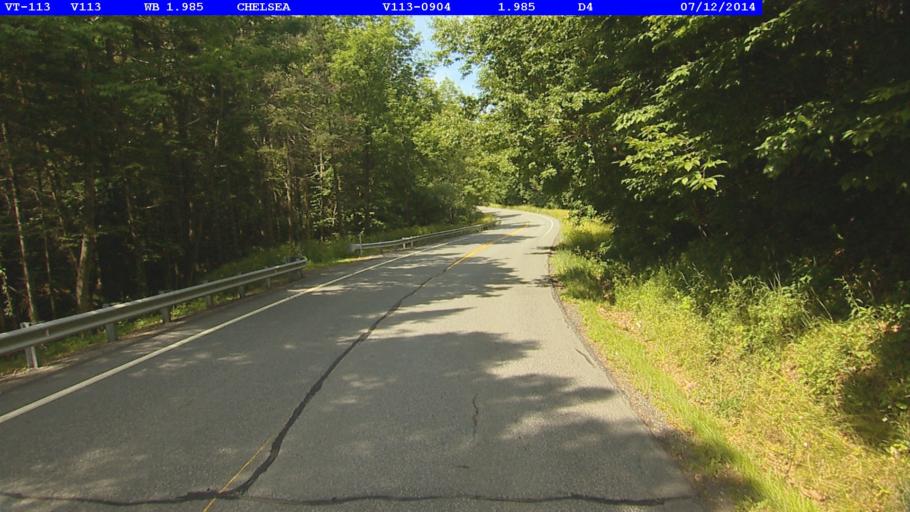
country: US
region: Vermont
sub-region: Orange County
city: Chelsea
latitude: 43.9901
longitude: -72.4128
